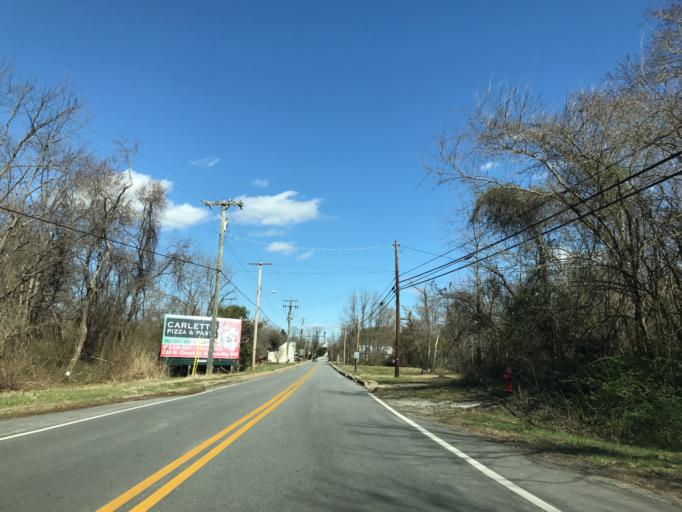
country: US
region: Delaware
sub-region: New Castle County
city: Townsend
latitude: 39.2540
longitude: -75.8430
